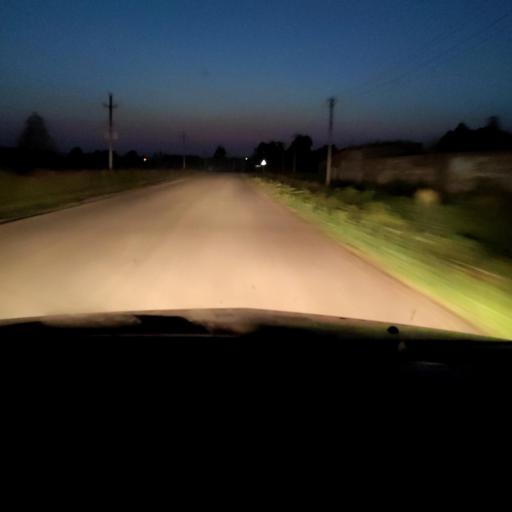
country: RU
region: Bashkortostan
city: Kabakovo
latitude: 54.6973
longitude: 56.2584
